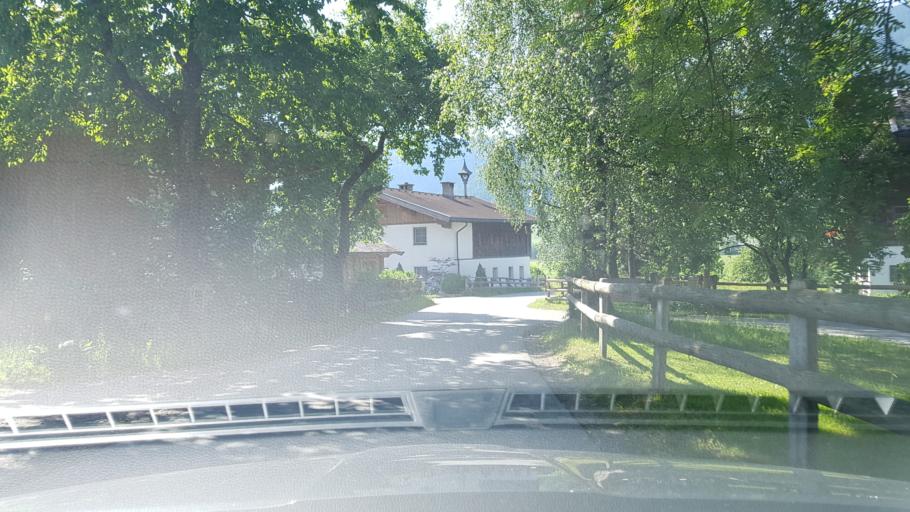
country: AT
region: Salzburg
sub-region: Politischer Bezirk Zell am See
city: Leogang
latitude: 47.4452
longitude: 12.7834
